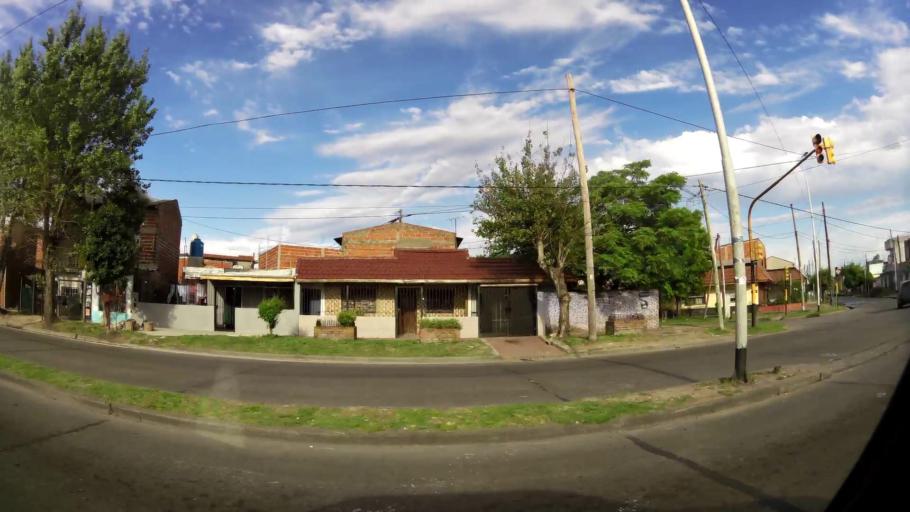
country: AR
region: Buenos Aires
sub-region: Partido de Lanus
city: Lanus
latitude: -34.7039
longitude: -58.3534
